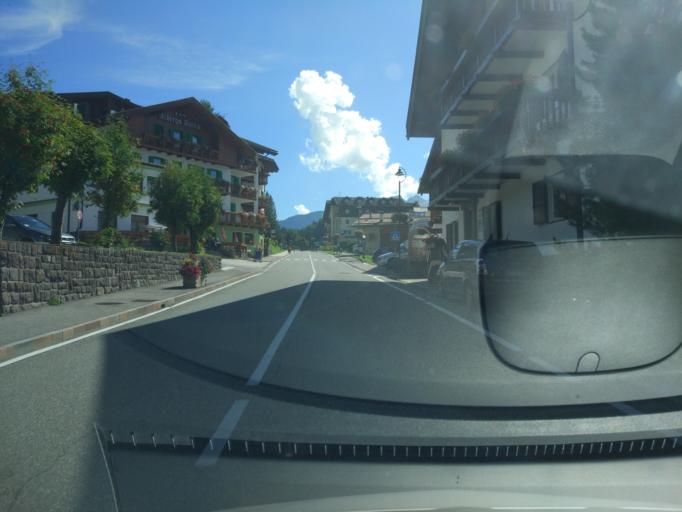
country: IT
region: Trentino-Alto Adige
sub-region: Provincia di Trento
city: Predazzo
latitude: 46.3132
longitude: 11.6620
